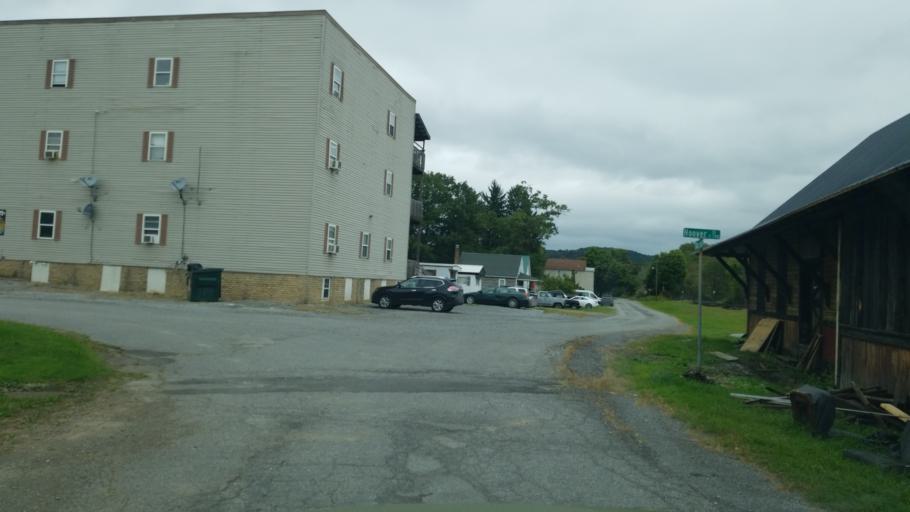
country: US
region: Pennsylvania
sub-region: Clearfield County
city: Hyde
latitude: 40.9994
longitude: -78.4637
